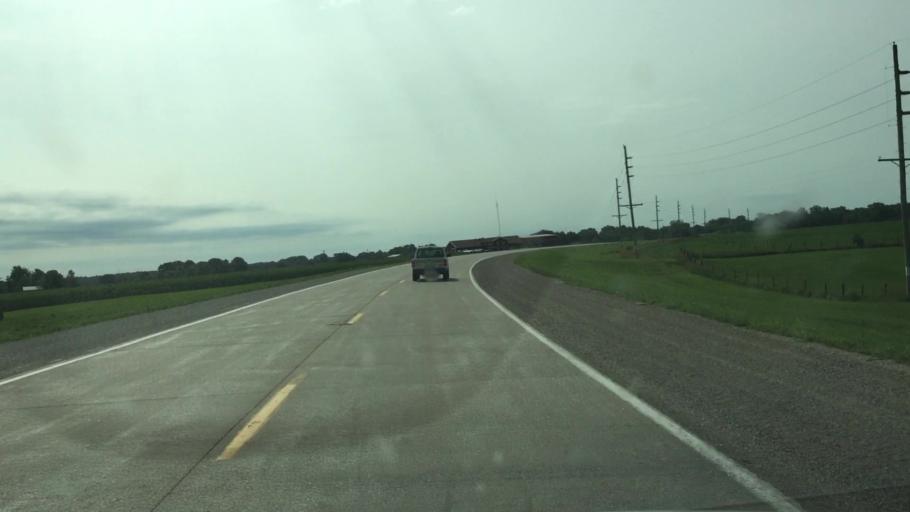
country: US
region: Illinois
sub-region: Hancock County
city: Nauvoo
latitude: 40.6385
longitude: -91.5225
